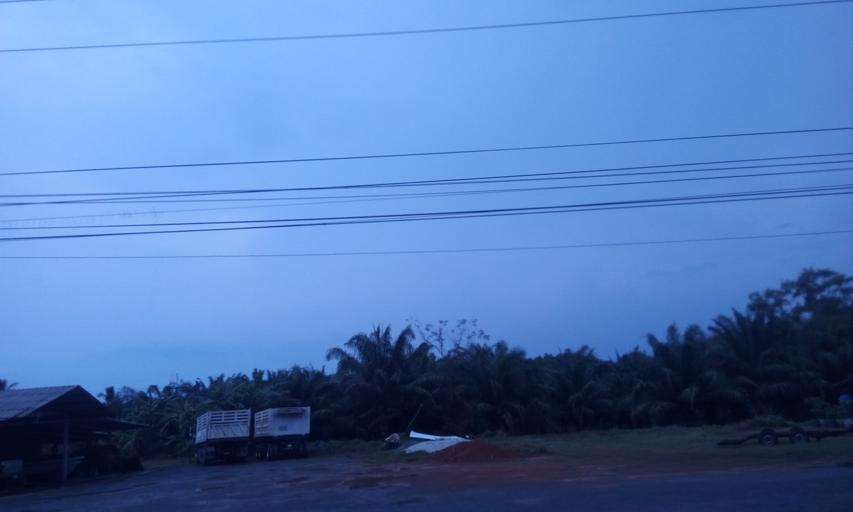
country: TH
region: Trat
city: Khao Saming
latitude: 12.3414
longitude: 102.3739
